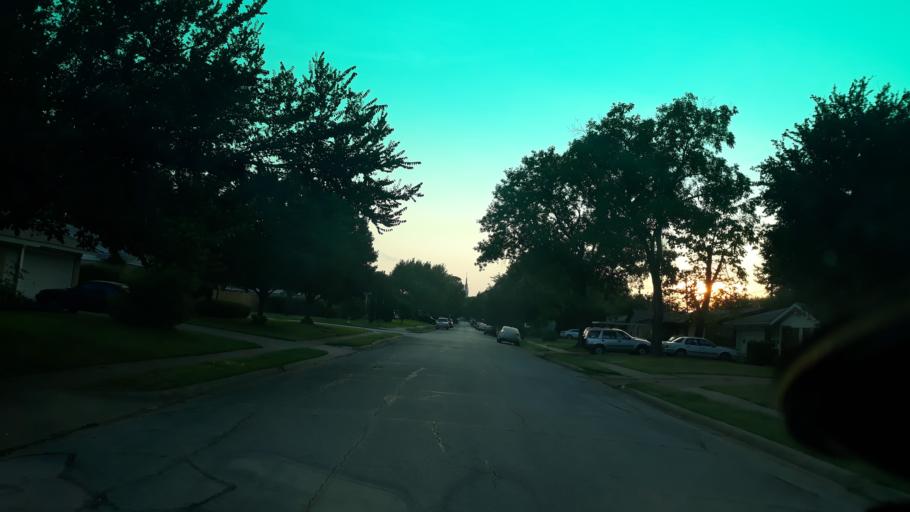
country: US
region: Texas
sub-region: Dallas County
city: Irving
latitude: 32.8363
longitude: -96.9798
